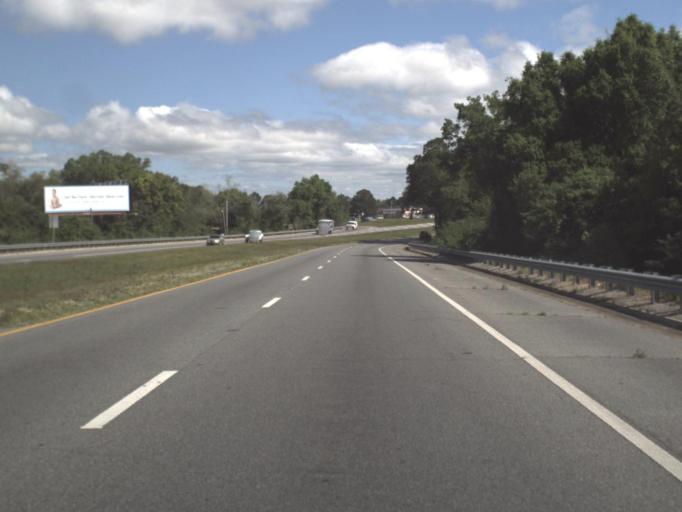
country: US
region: Florida
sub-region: Escambia County
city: West Pensacola
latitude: 30.4270
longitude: -87.2745
